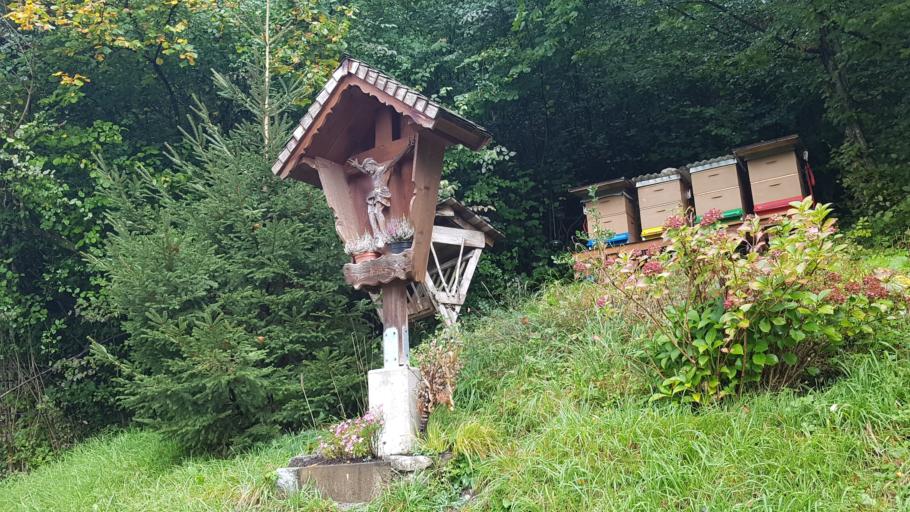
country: AT
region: Salzburg
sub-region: Politischer Bezirk Hallein
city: Puch bei Hallein
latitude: 47.7325
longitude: 13.0978
